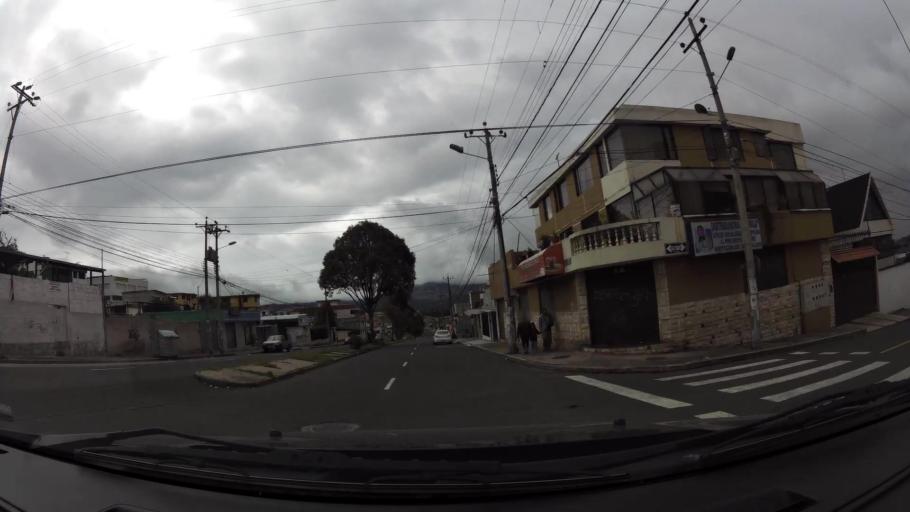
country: EC
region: Pichincha
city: Quito
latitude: -0.1214
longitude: -78.5023
